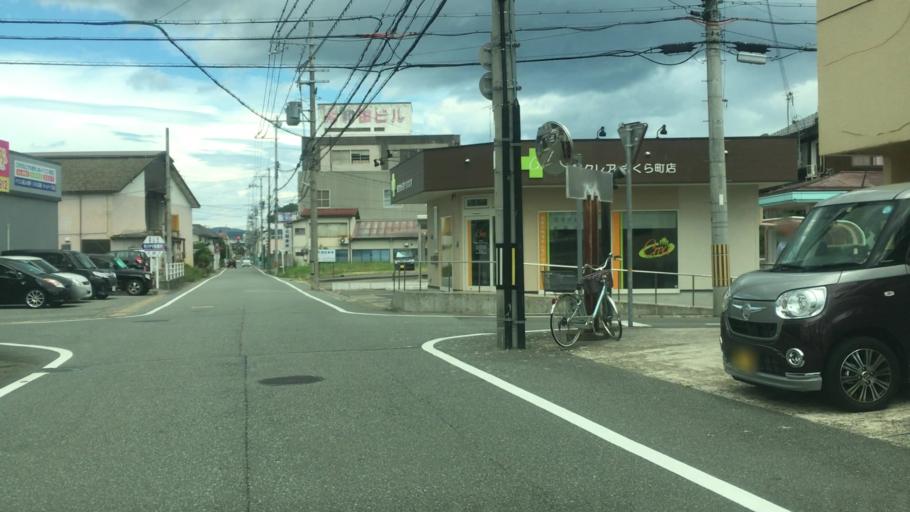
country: JP
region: Hyogo
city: Toyooka
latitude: 35.5332
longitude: 134.8207
